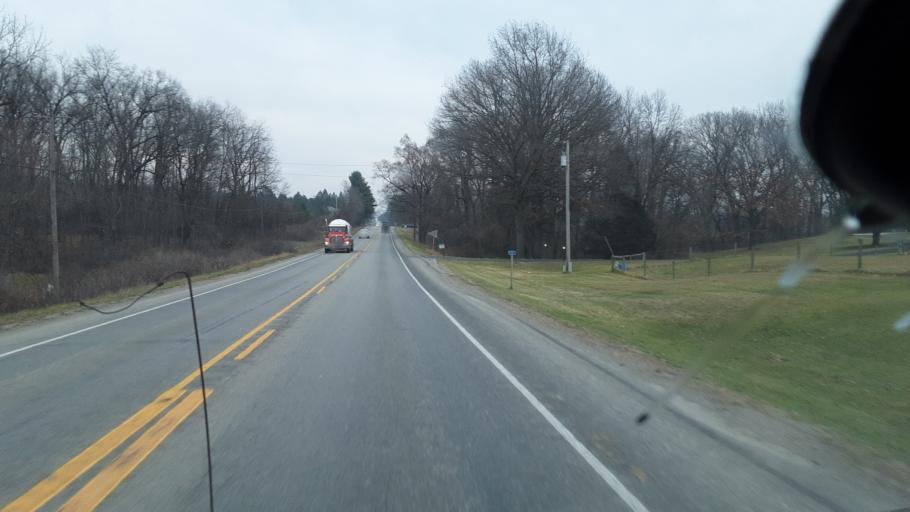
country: US
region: Indiana
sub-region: Elkhart County
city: Middlebury
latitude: 41.7257
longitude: -85.6806
